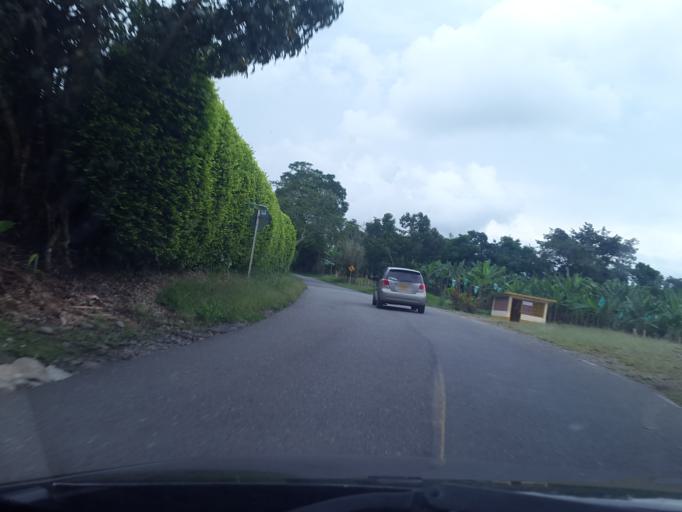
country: CO
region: Quindio
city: La Tebaida
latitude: 4.4972
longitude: -75.7960
